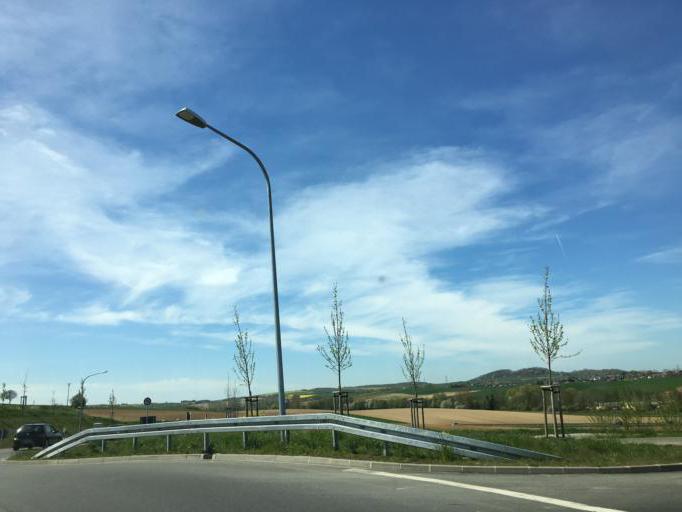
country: DE
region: Hesse
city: Reinheim
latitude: 49.8348
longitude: 8.8233
